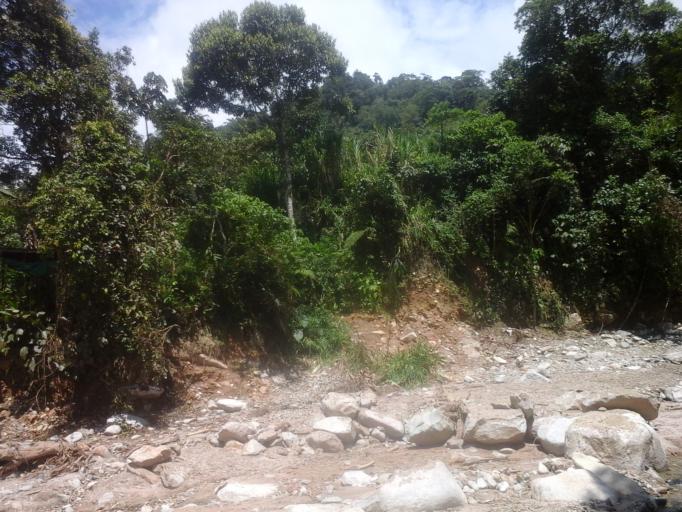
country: CO
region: Putumayo
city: Mocoa
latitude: 1.1832
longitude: -76.6779
